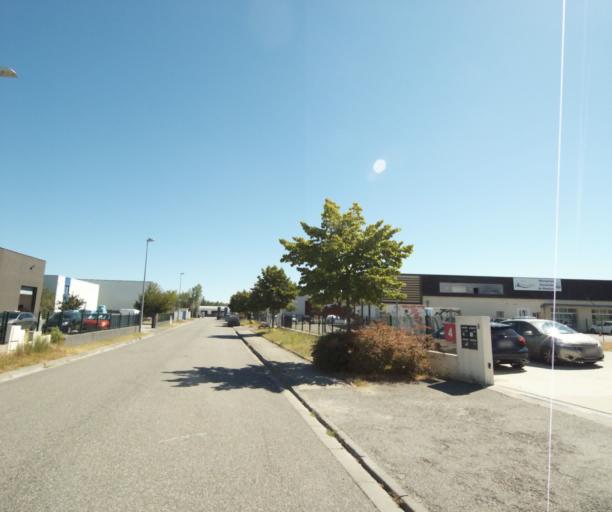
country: FR
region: Midi-Pyrenees
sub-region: Departement de la Haute-Garonne
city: Pechabou
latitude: 43.5133
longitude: 1.5229
